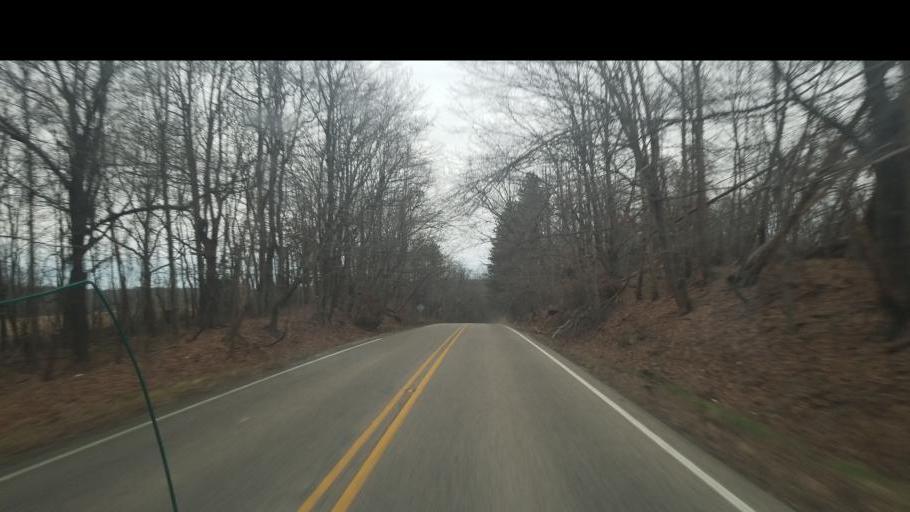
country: US
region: Indiana
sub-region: Owen County
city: Spencer
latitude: 39.3567
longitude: -86.9397
